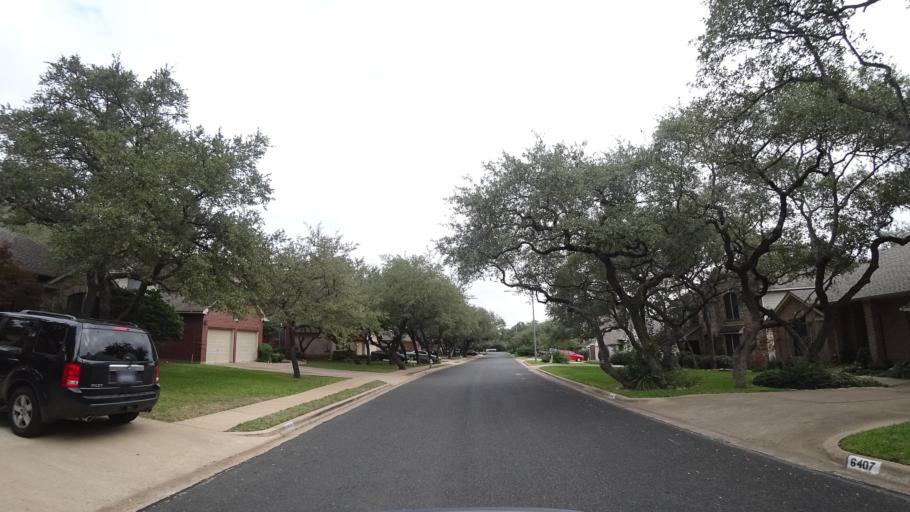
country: US
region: Texas
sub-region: Travis County
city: Shady Hollow
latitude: 30.2142
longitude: -97.8787
